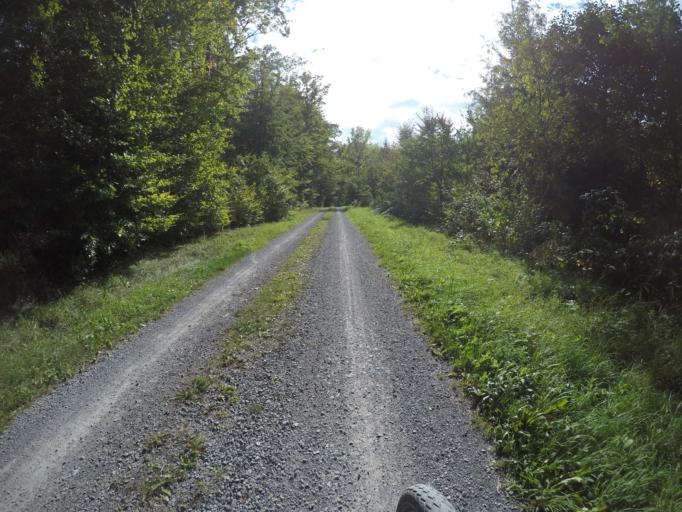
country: DE
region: Baden-Wuerttemberg
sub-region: Regierungsbezirk Stuttgart
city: Hildrizhausen
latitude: 48.6139
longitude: 8.9321
